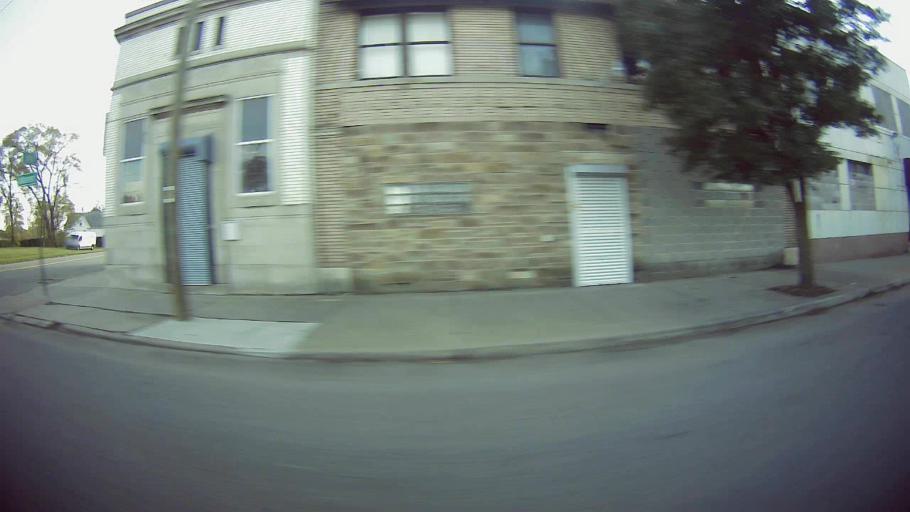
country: US
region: Michigan
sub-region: Wayne County
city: Dearborn
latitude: 42.3446
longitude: -83.1164
